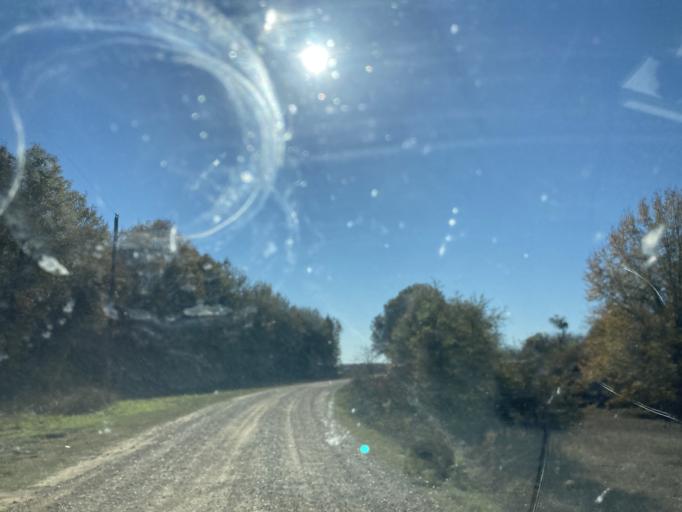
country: US
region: Mississippi
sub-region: Sharkey County
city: Rolling Fork
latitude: 32.7573
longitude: -90.6888
